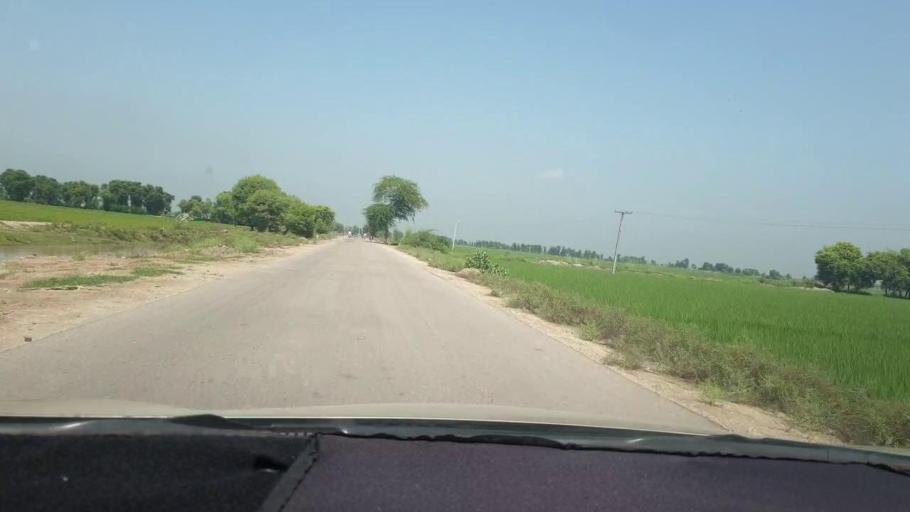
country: PK
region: Sindh
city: Miro Khan
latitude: 27.7646
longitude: 68.0735
